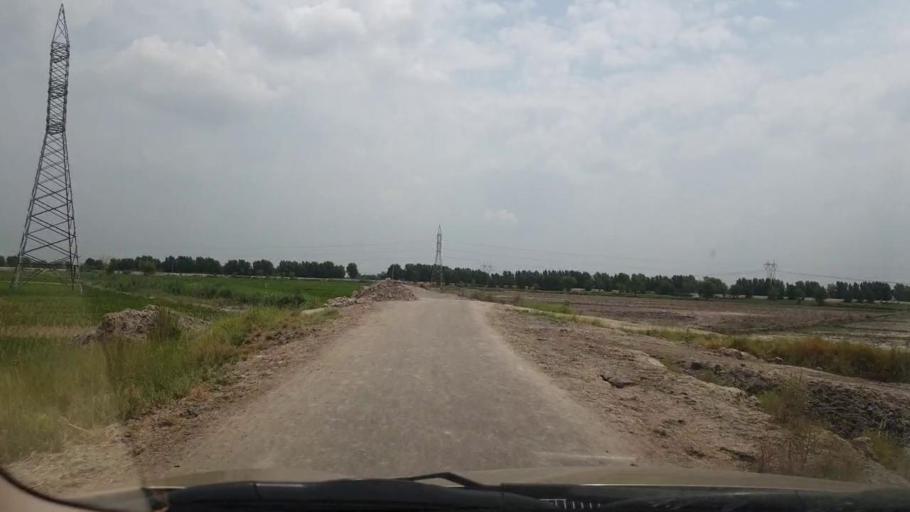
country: PK
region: Sindh
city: Larkana
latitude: 27.5443
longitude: 68.1567
